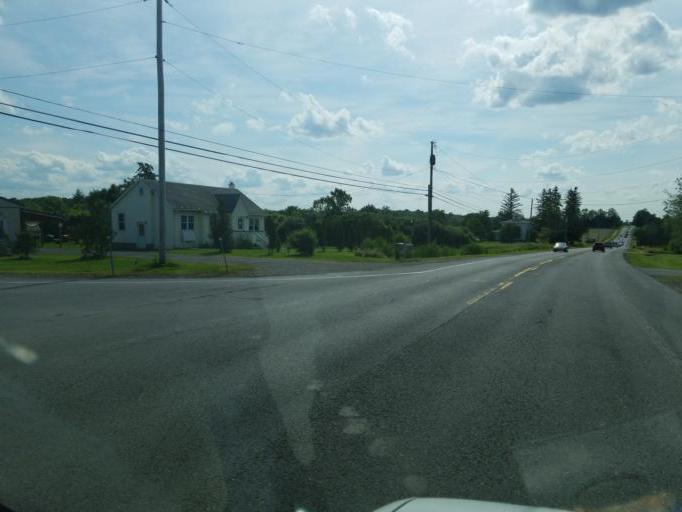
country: US
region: New York
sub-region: Ontario County
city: Clifton Springs
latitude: 42.8606
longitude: -77.1682
